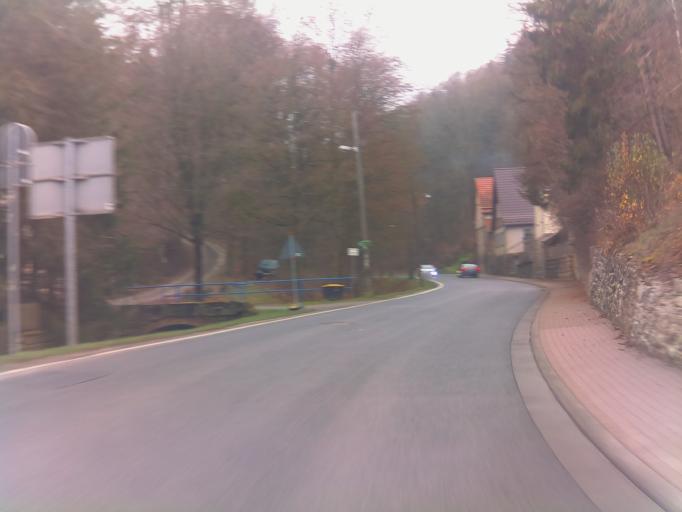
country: DE
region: Thuringia
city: Themar
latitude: 50.5005
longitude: 10.6108
